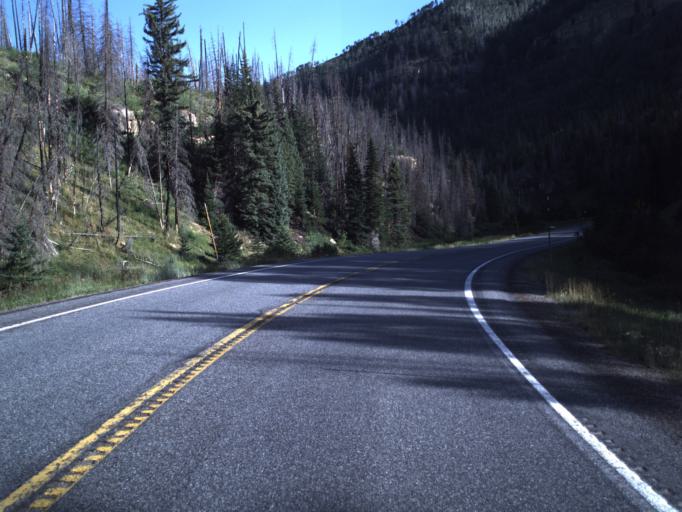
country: US
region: Utah
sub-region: Sanpete County
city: Fairview
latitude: 39.5838
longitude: -111.1928
